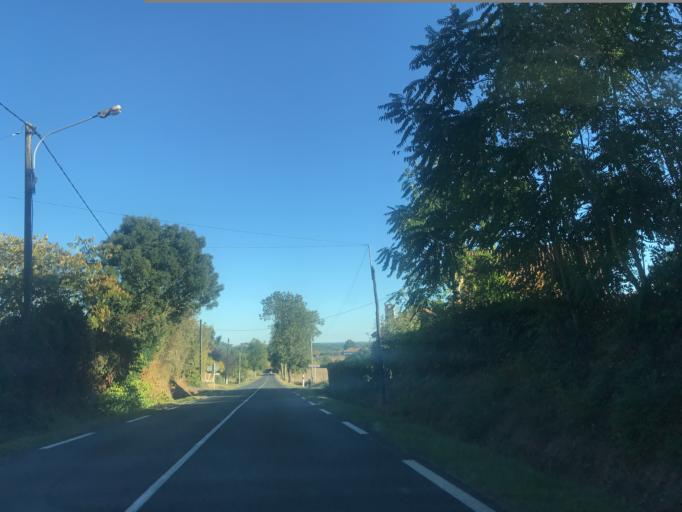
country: FR
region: Poitou-Charentes
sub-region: Departement de la Charente-Maritime
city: Montguyon
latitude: 45.1777
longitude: -0.1175
